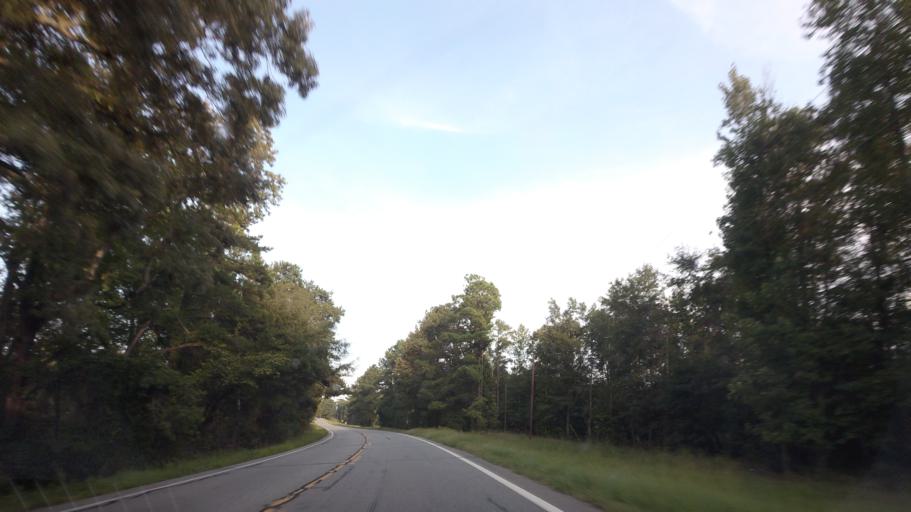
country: US
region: Georgia
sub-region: Wilkinson County
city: Gordon
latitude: 32.8595
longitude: -83.3599
